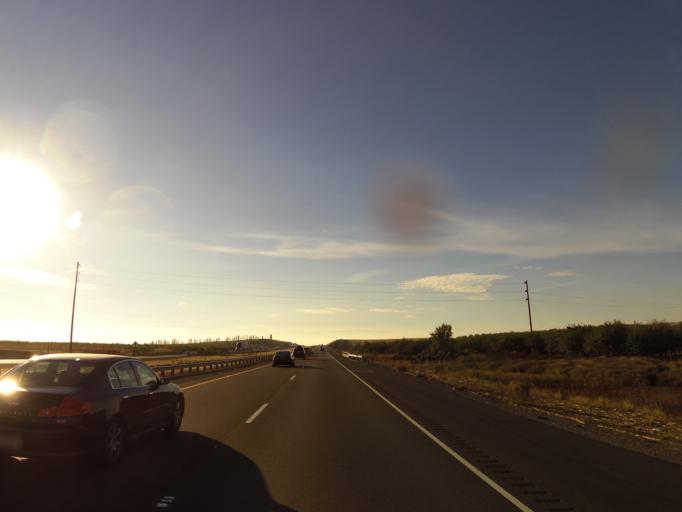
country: US
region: California
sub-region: Stanislaus County
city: Patterson
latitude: 37.3750
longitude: -121.1263
